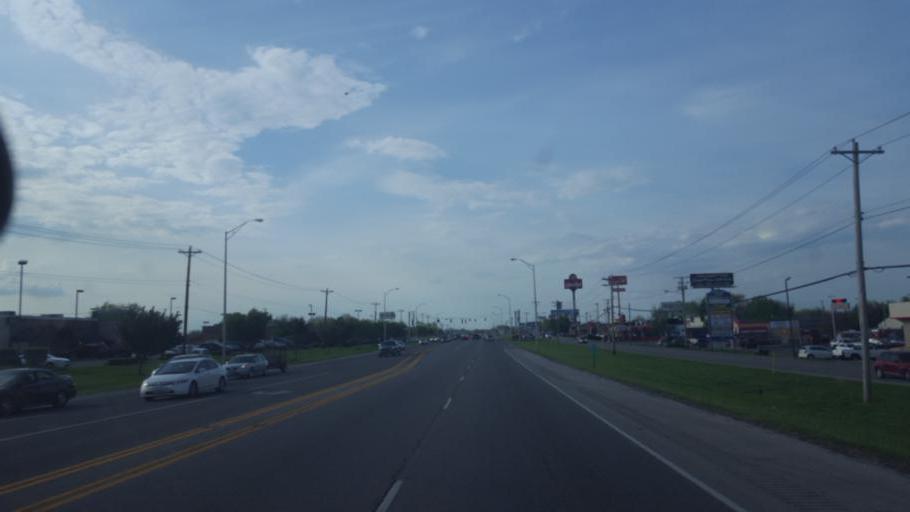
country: US
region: Kentucky
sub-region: Warren County
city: Bowling Green
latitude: 36.9469
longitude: -86.4235
